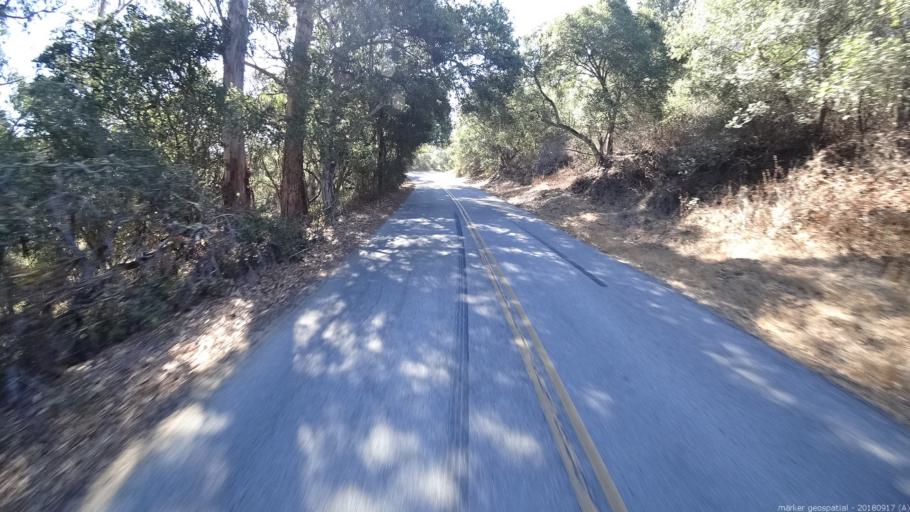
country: US
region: California
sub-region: Monterey County
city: Elkhorn
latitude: 36.8279
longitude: -121.7324
